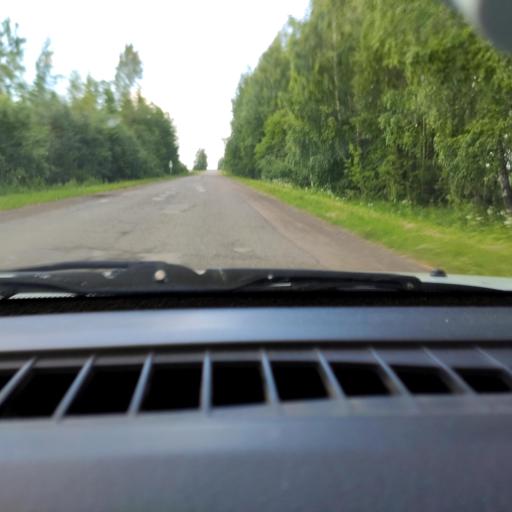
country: RU
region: Perm
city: Kukushtan
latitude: 57.2814
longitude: 56.5356
